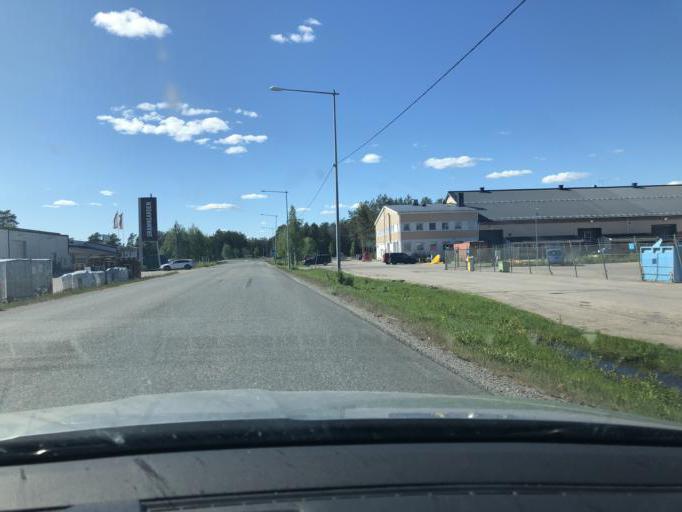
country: SE
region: Norrbotten
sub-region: Kalix Kommun
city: Kalix
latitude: 65.8627
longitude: 23.1434
